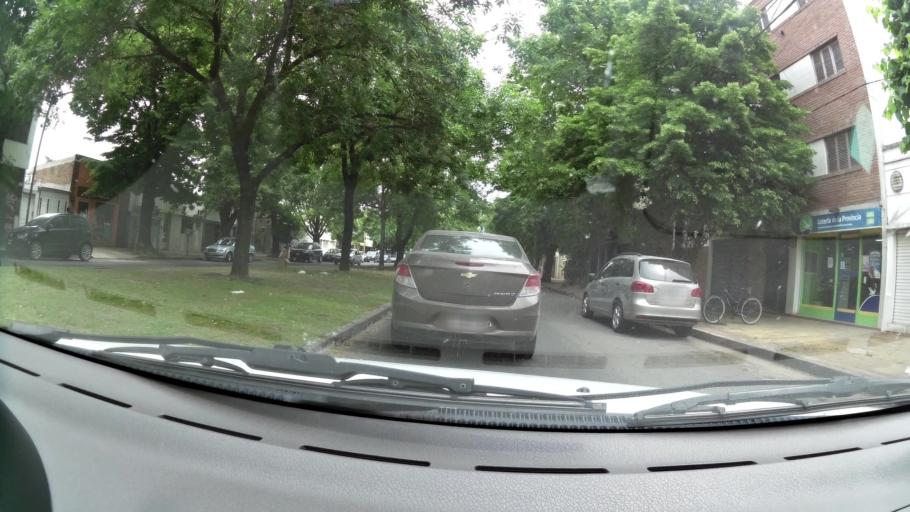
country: AR
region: Buenos Aires
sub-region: Partido de La Plata
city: La Plata
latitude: -34.9425
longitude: -57.9654
